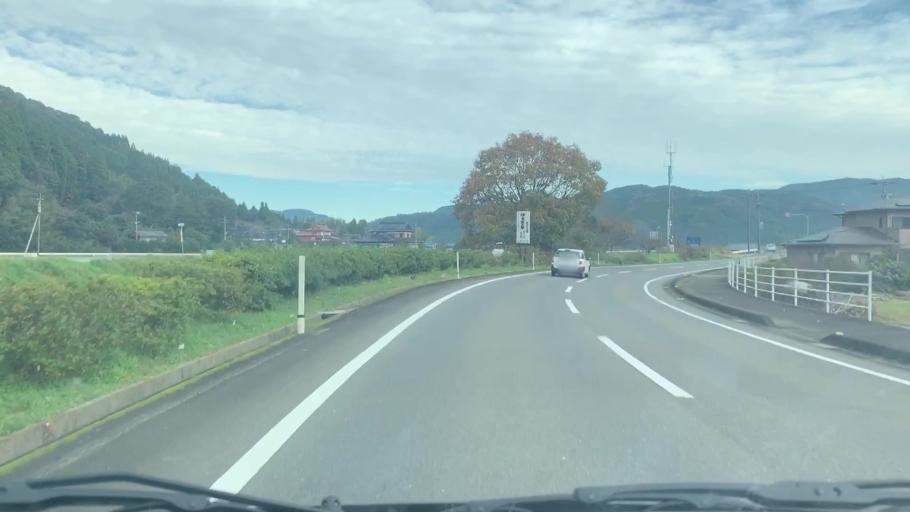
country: JP
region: Saga Prefecture
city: Imaricho-ko
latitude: 33.3072
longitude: 129.9690
